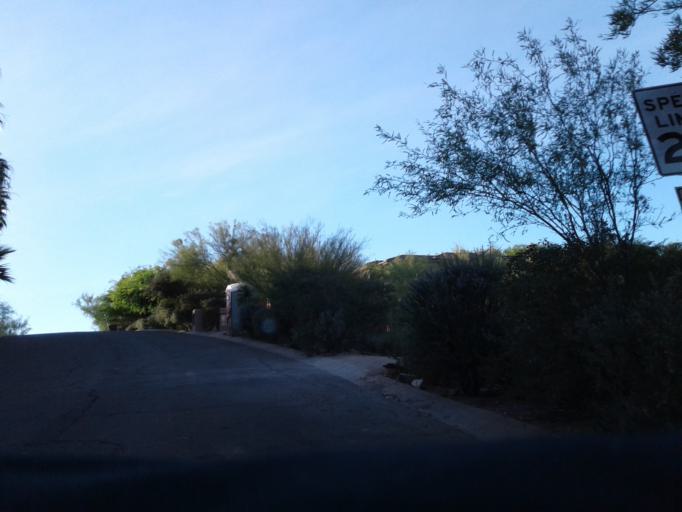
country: US
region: Arizona
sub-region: Maricopa County
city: Paradise Valley
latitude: 33.5275
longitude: -111.9959
